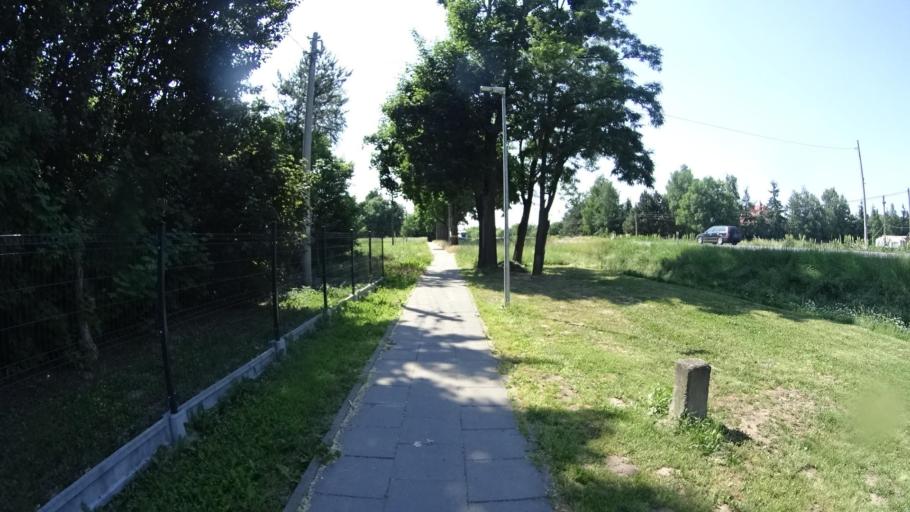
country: PL
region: Masovian Voivodeship
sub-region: Powiat warszawski zachodni
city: Bieniewice
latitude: 52.1999
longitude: 20.5789
